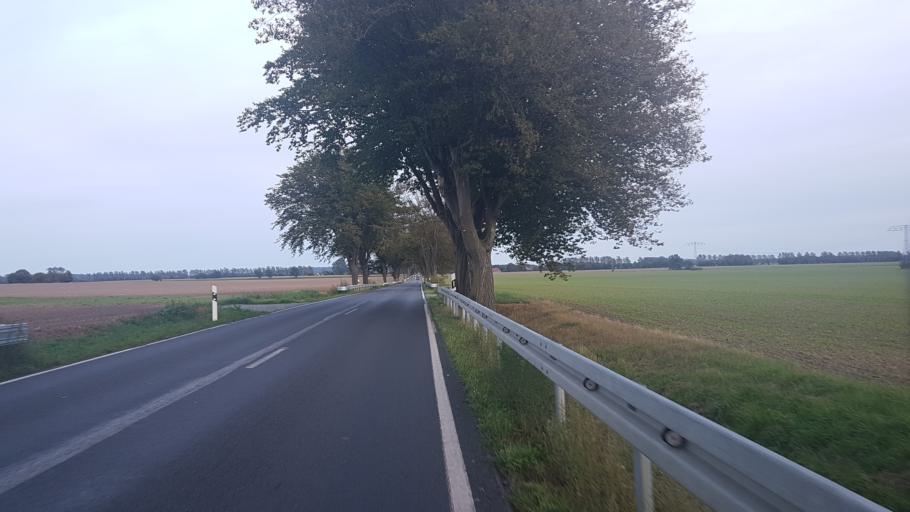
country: DE
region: Mecklenburg-Vorpommern
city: Sehlen
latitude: 54.4464
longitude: 13.3572
